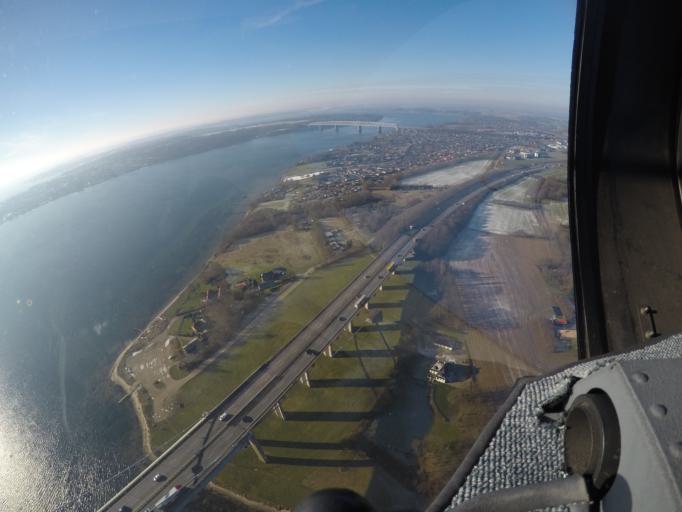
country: DK
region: South Denmark
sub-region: Middelfart Kommune
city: Middelfart
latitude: 55.5210
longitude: 9.7423
